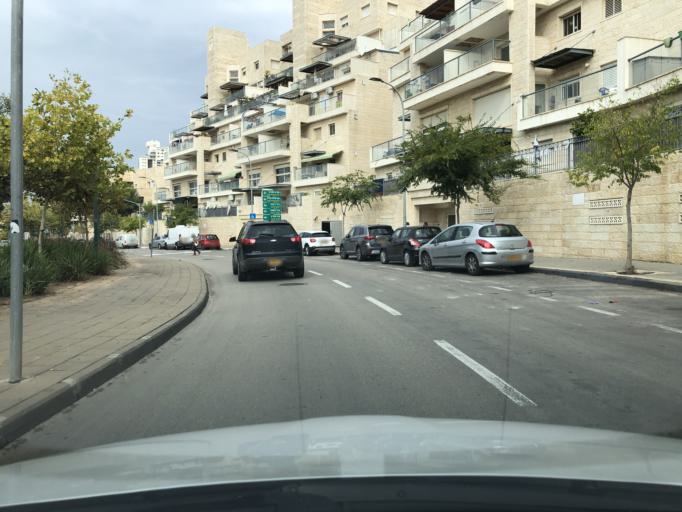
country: IL
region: Central District
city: Modiin
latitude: 31.9119
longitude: 35.0126
